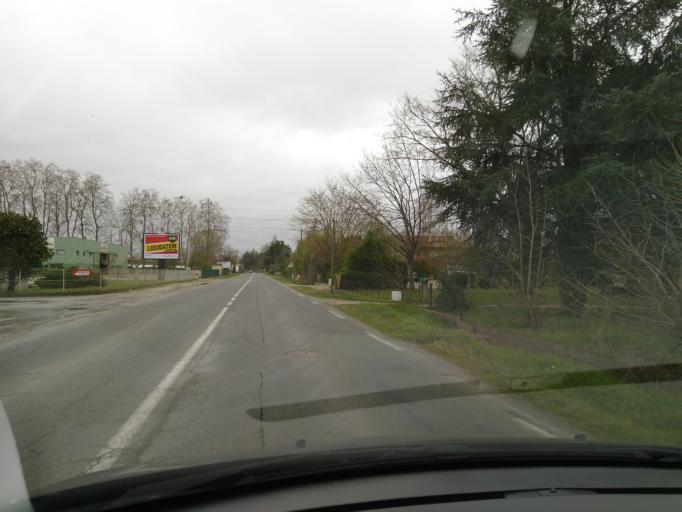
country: FR
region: Aquitaine
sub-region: Departement de la Dordogne
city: Bergerac
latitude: 44.8332
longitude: 0.4965
